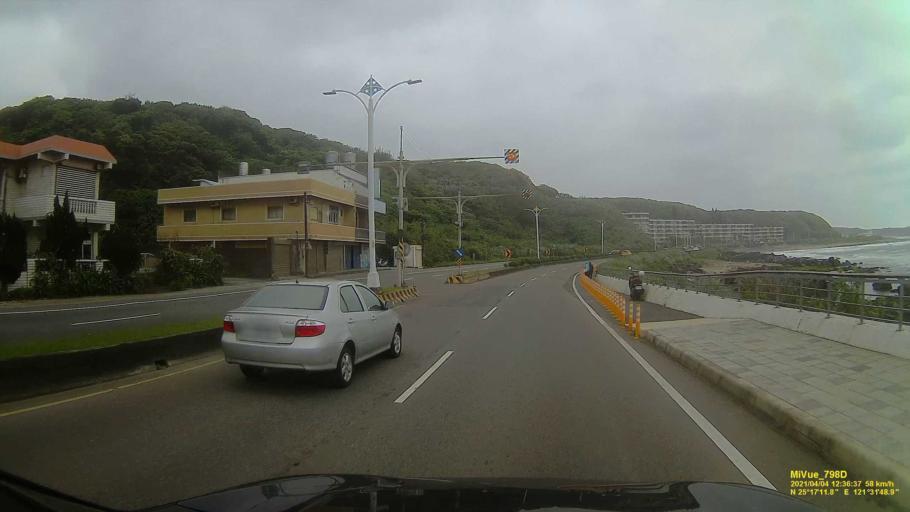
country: TW
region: Taipei
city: Taipei
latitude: 25.2864
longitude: 121.5300
